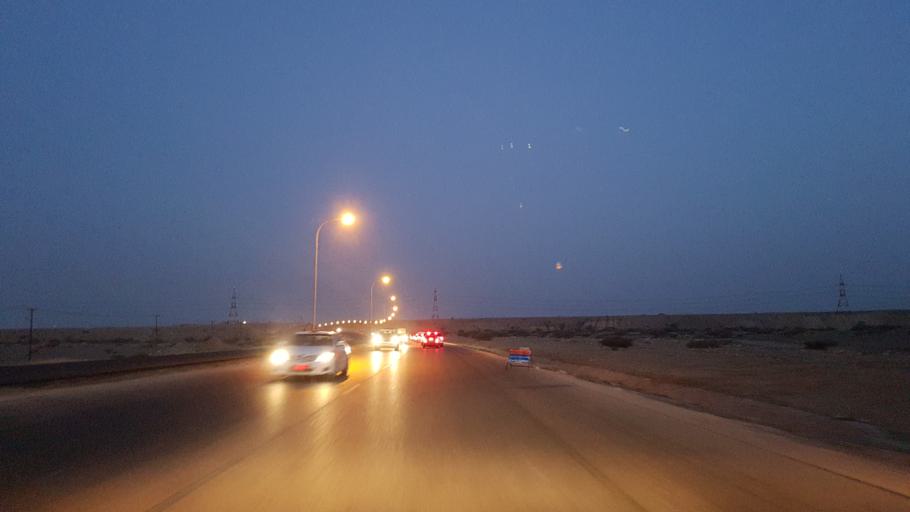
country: OM
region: Ash Sharqiyah
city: Sur
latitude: 22.5885
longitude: 59.4411
